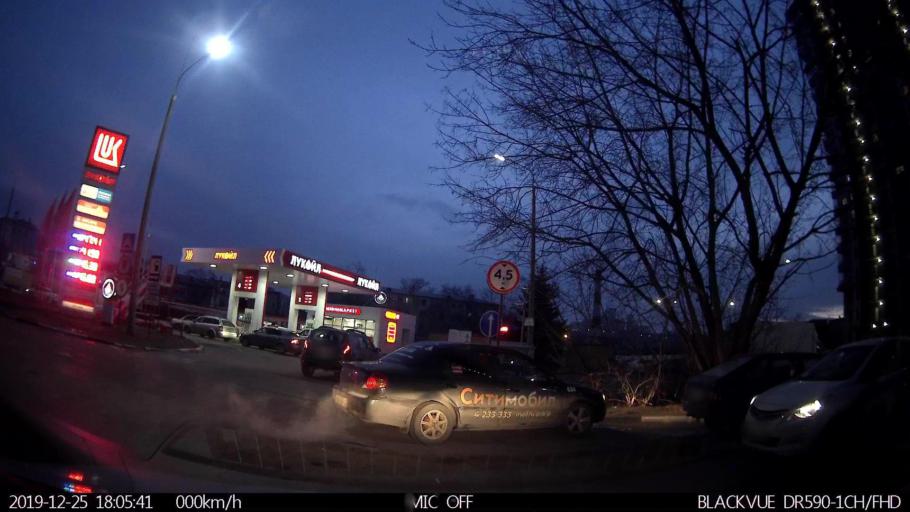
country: RU
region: Nizjnij Novgorod
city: Nizhniy Novgorod
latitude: 56.3092
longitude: 43.9461
